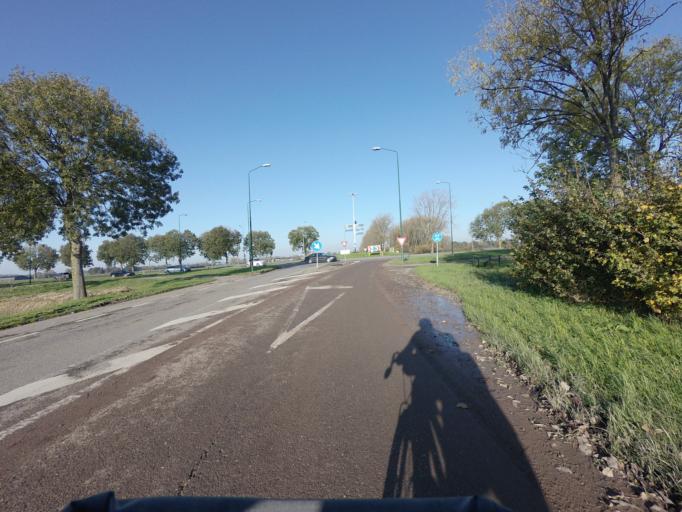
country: NL
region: North Brabant
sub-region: Gemeente Woudrichem
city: Woudrichem
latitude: 51.7730
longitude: 5.0491
